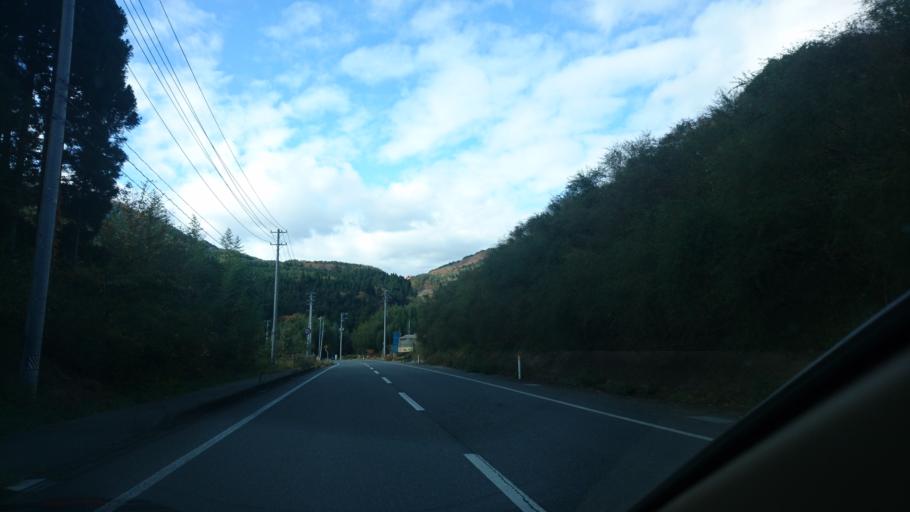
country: JP
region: Iwate
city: Ofunato
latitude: 39.0275
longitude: 141.7075
